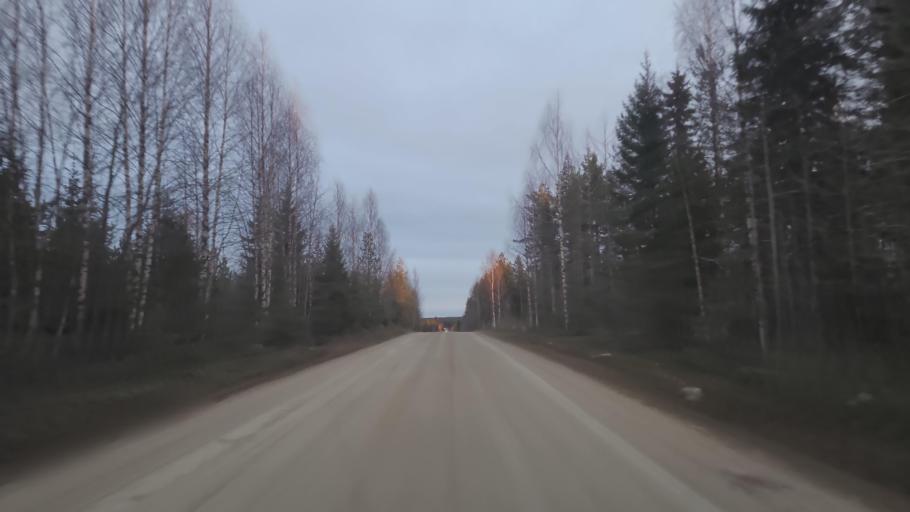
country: FI
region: Lapland
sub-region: Kemi-Tornio
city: Tervola
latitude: 66.0575
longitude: 24.9455
